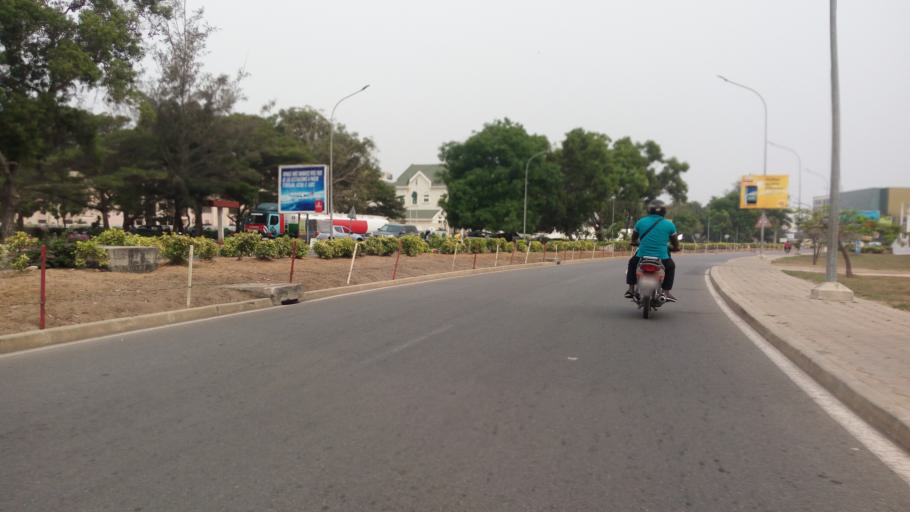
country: BJ
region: Littoral
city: Cotonou
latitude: 6.3503
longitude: 2.3938
